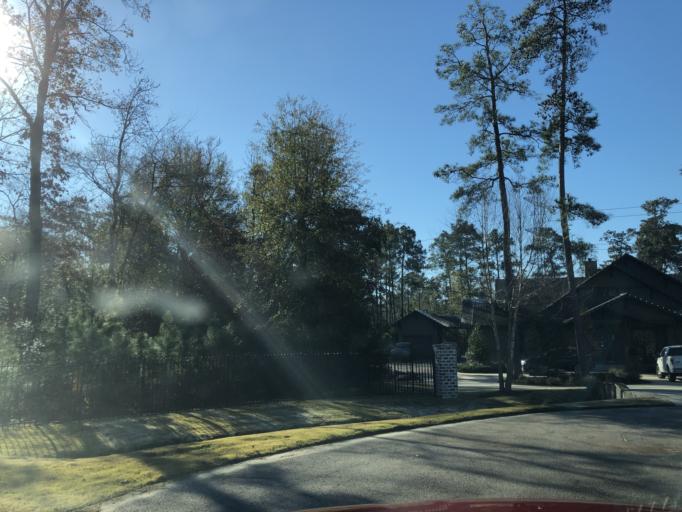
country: US
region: Texas
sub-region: Montgomery County
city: Porter Heights
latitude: 30.0707
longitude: -95.3352
